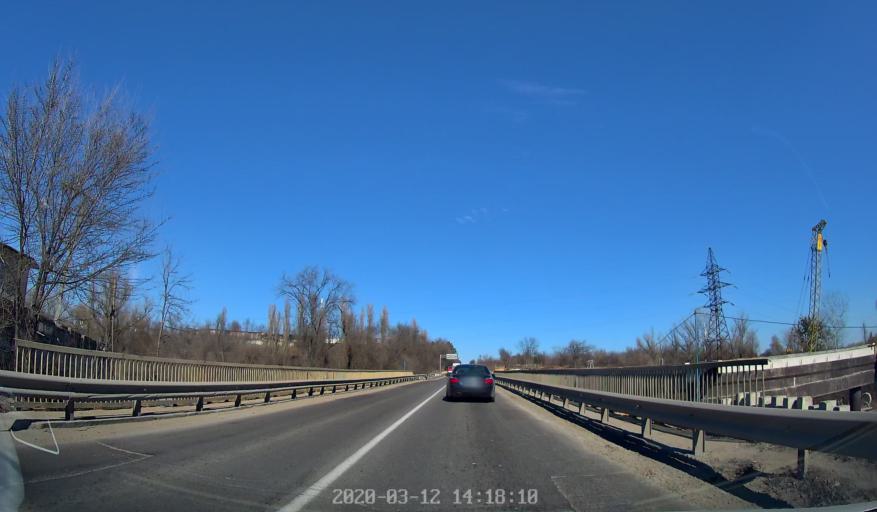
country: MD
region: Chisinau
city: Vatra
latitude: 47.0547
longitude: 28.7791
